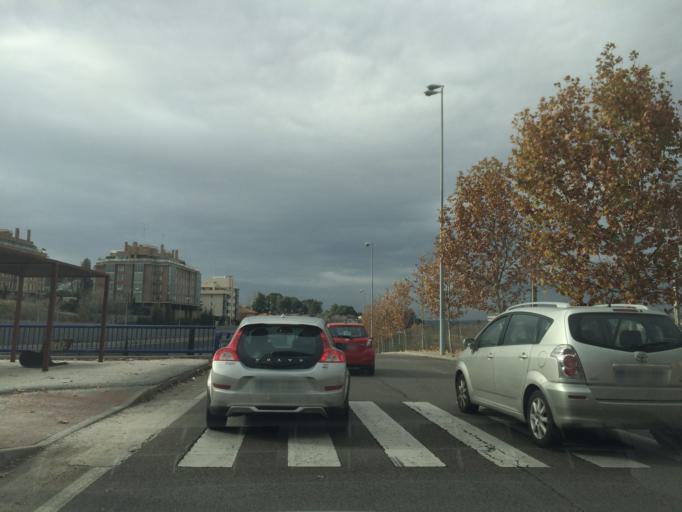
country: ES
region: Madrid
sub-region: Provincia de Madrid
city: Tetuan de las Victorias
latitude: 40.4731
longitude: -3.7287
